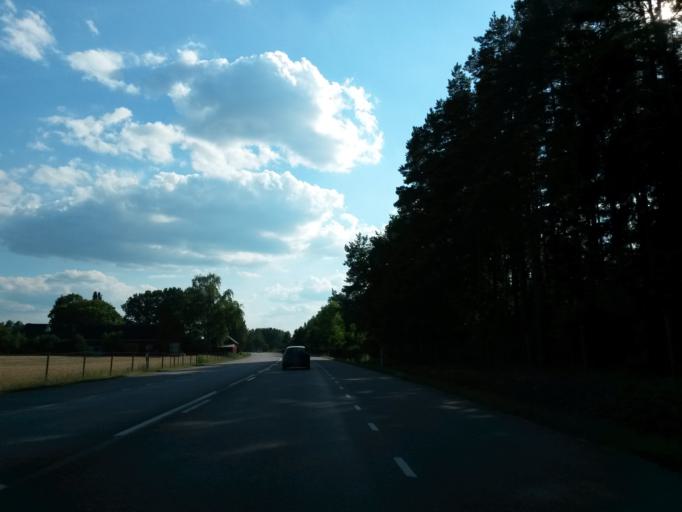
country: SE
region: Vaestra Goetaland
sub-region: Vara Kommun
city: Vara
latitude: 58.2115
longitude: 12.9059
